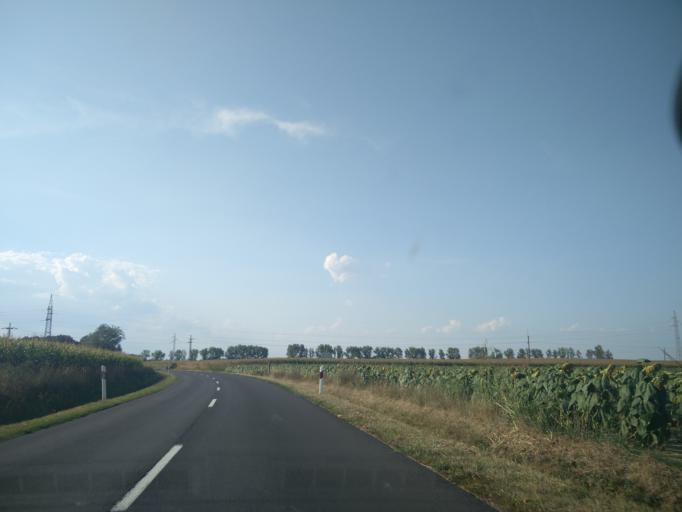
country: HU
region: Zala
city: Zalaegerszeg
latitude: 46.8607
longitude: 16.8381
